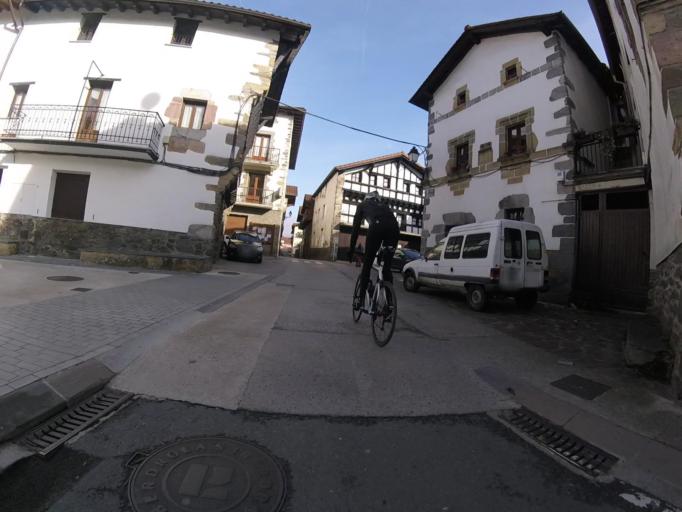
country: ES
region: Navarre
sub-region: Provincia de Navarra
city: Goizueta
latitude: 43.1712
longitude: -1.8639
